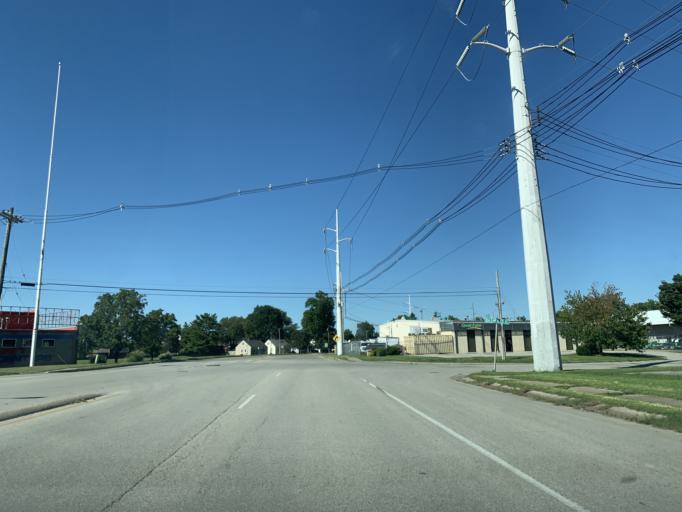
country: US
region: Kentucky
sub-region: Jefferson County
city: West Buechel
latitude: 38.1937
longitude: -85.6659
